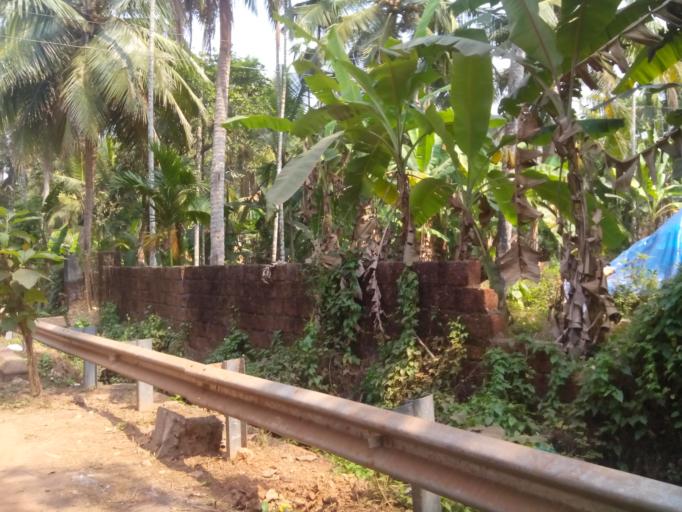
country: IN
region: Kerala
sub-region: Kozhikode
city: Naduvannur
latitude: 11.5840
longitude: 75.7635
